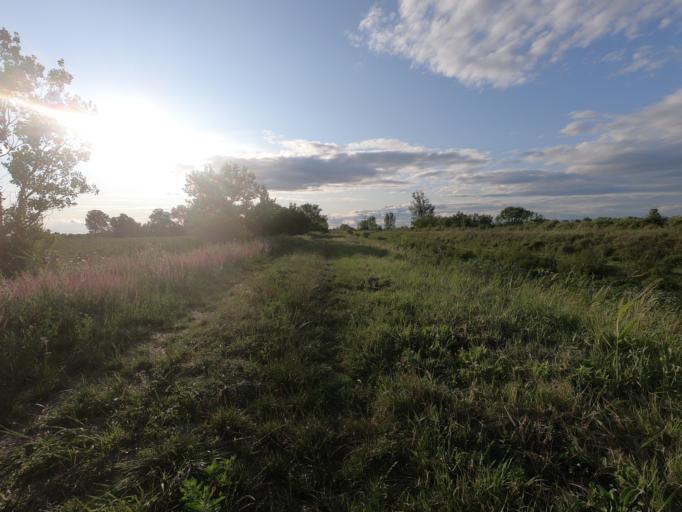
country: HU
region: Heves
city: Szihalom
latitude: 47.7191
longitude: 20.5648
